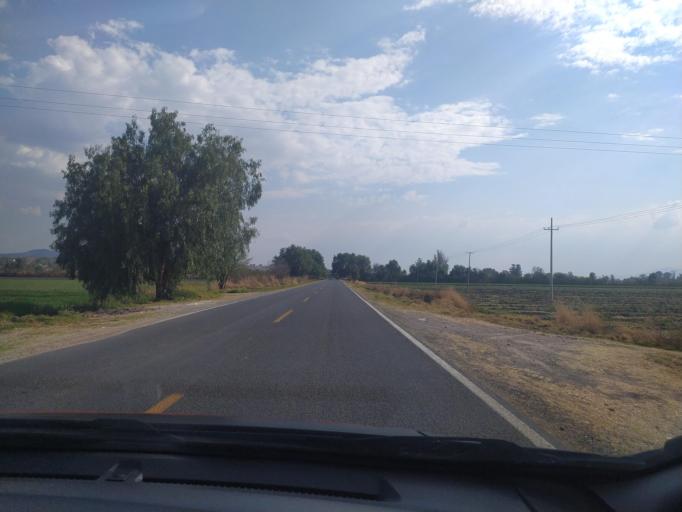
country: MX
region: Guanajuato
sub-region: San Francisco del Rincon
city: San Ignacio de Hidalgo
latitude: 20.8928
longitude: -101.8578
